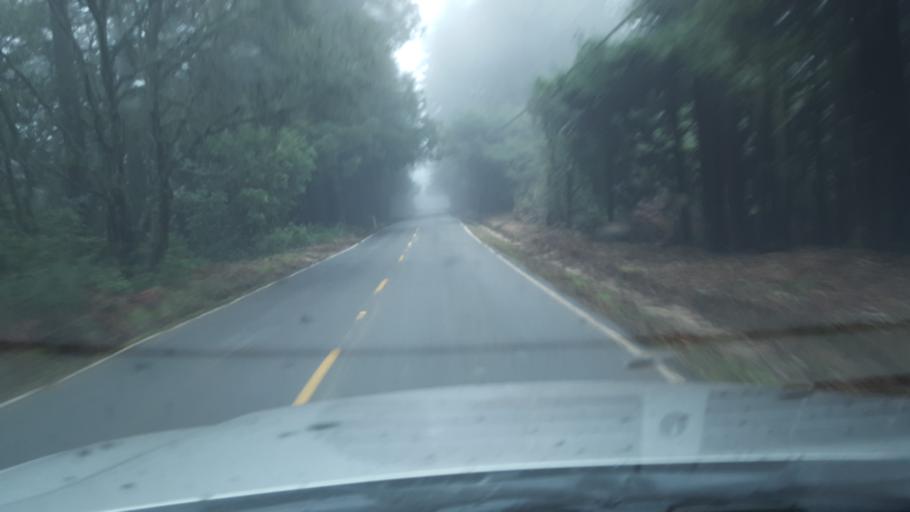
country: US
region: California
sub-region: Santa Cruz County
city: Interlaken
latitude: 37.0238
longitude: -121.7307
